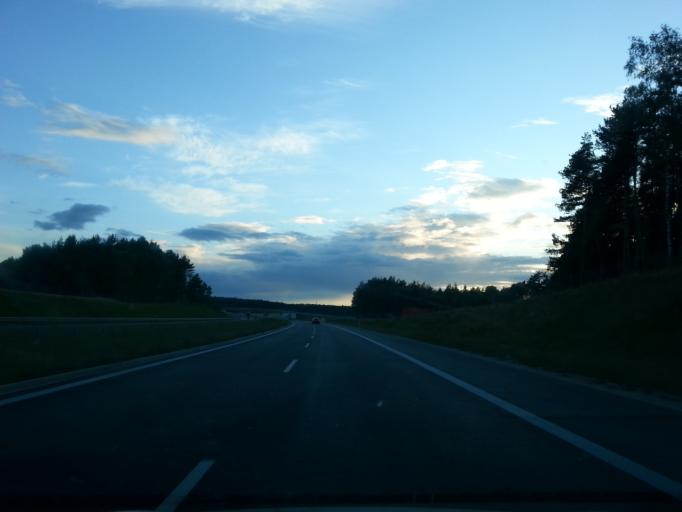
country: PL
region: Greater Poland Voivodeship
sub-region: Powiat kepinski
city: Perzow
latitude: 51.3039
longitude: 17.7882
